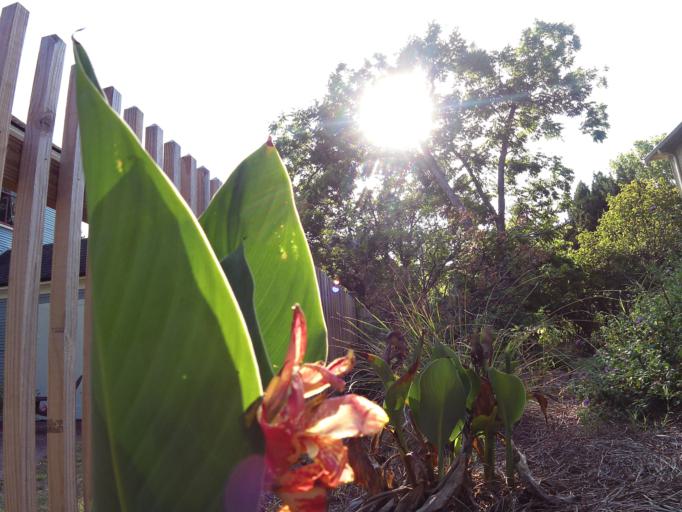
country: US
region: Florida
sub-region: Nassau County
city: Fernandina Beach
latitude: 30.6727
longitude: -81.4611
